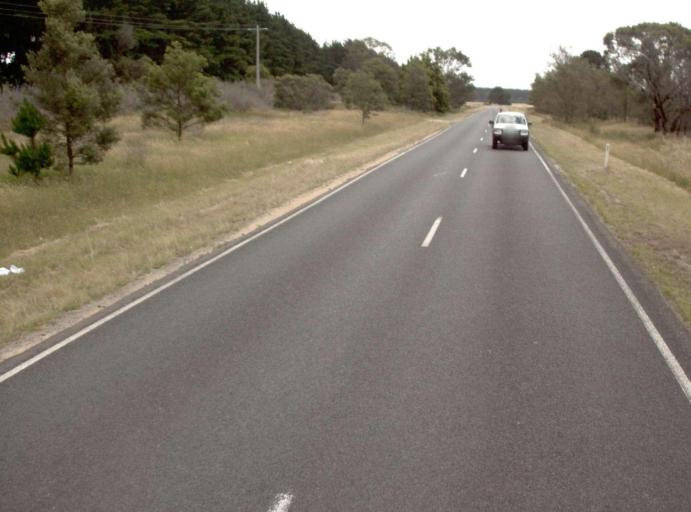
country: AU
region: Victoria
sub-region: Wellington
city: Sale
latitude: -38.1649
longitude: 147.0472
